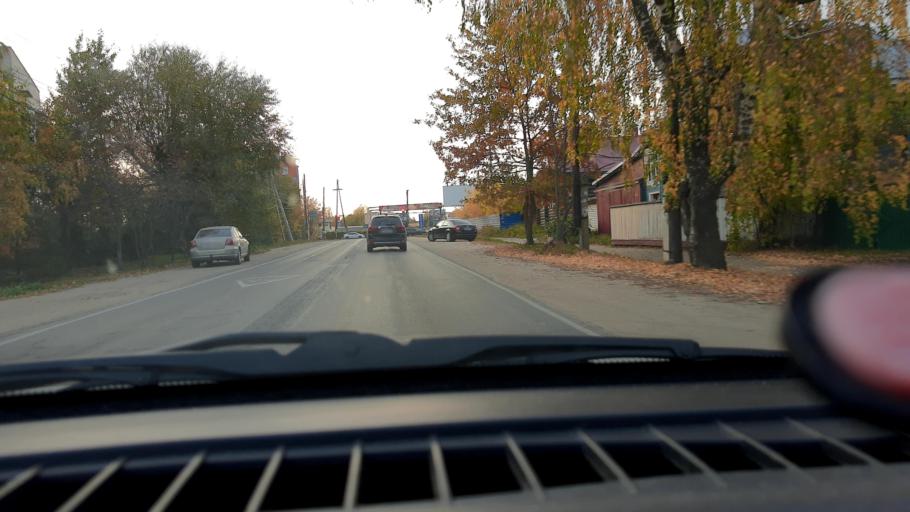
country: RU
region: Nizjnij Novgorod
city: Gorodets
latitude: 56.6404
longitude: 43.4805
